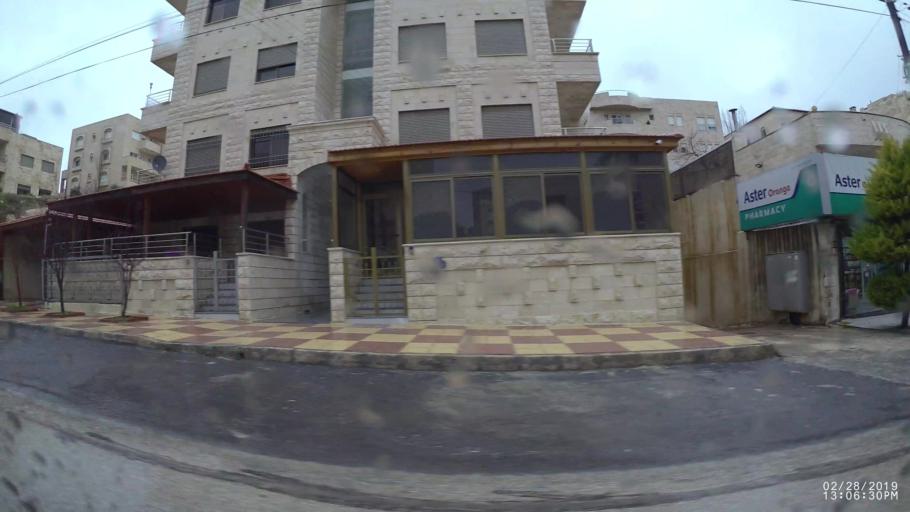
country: JO
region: Amman
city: Al Jubayhah
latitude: 32.0236
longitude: 35.8819
